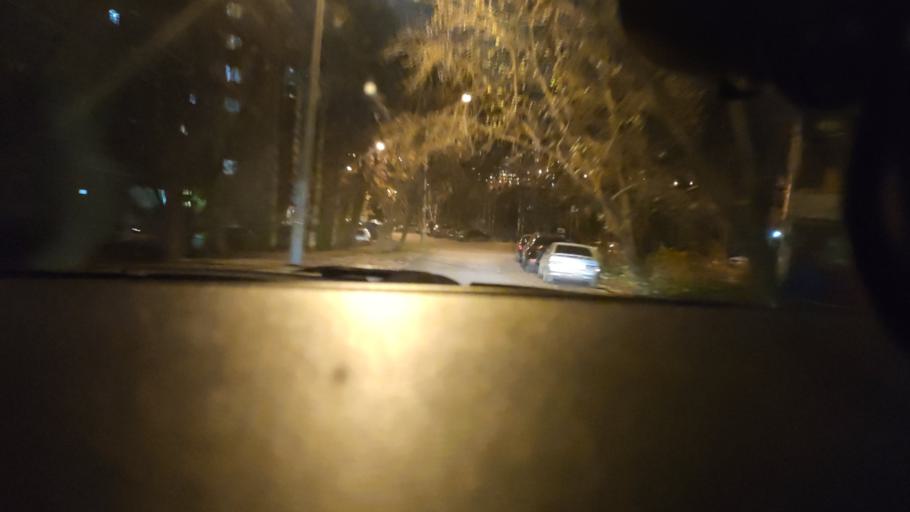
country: RU
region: Perm
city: Perm
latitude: 57.9810
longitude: 56.2322
